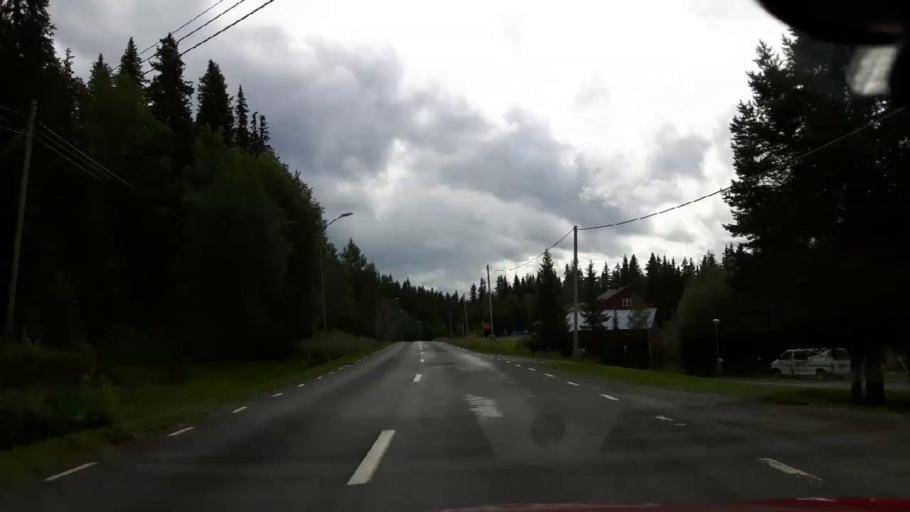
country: NO
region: Nord-Trondelag
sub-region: Lierne
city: Sandvika
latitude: 64.5054
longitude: 14.1570
